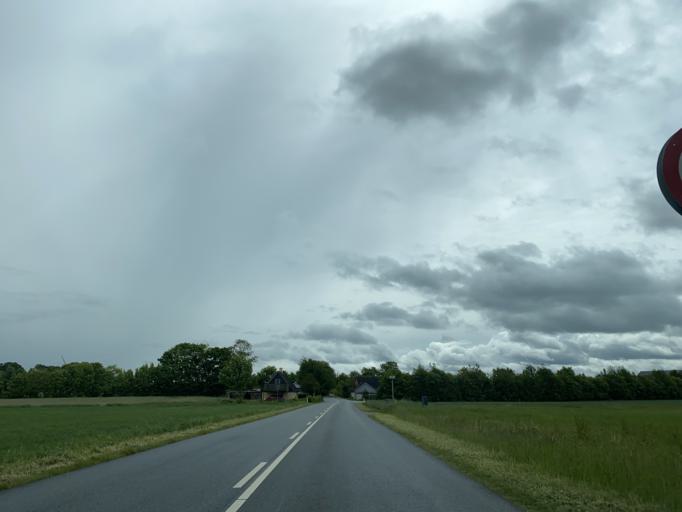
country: DK
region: Central Jutland
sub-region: Arhus Kommune
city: Sabro
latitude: 56.2548
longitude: 9.9657
